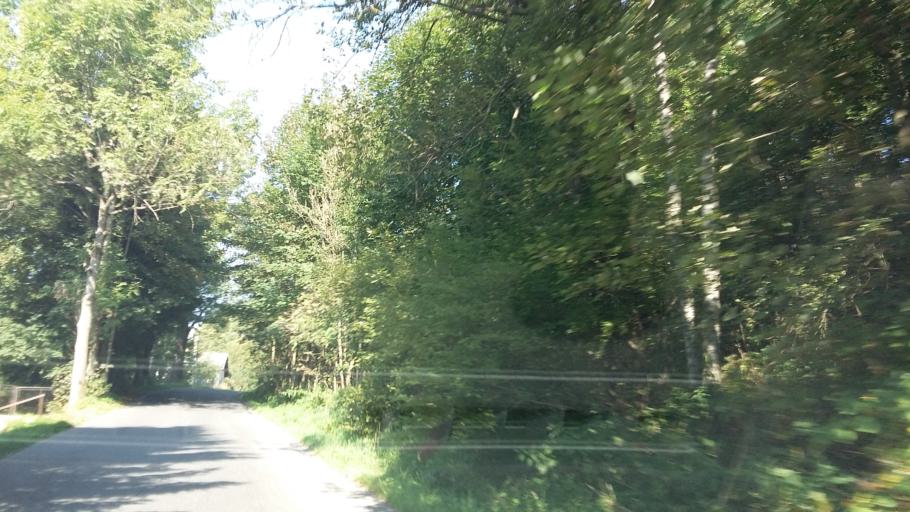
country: CZ
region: Liberecky
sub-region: Okres Jablonec nad Nisou
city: Janov nad Nisou
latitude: 50.7697
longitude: 15.1895
